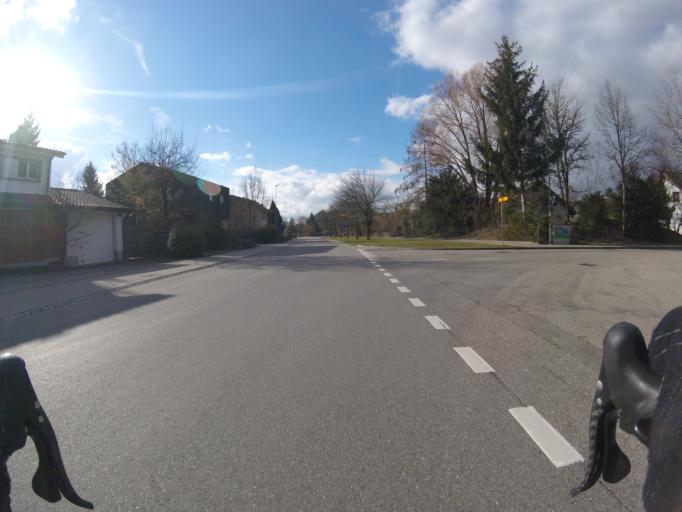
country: CH
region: Bern
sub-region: Bern-Mittelland District
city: Kirchlindach
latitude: 46.9749
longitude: 7.4267
